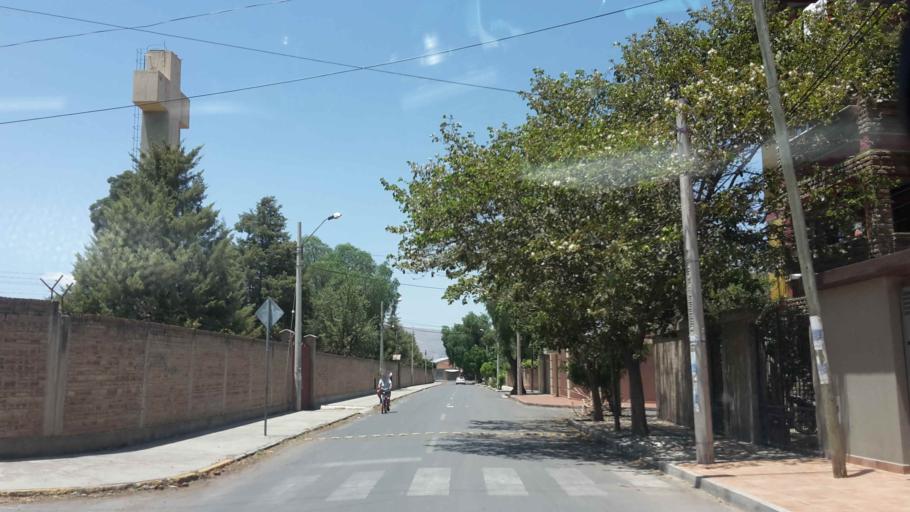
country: BO
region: Cochabamba
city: Cochabamba
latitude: -17.3800
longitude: -66.1930
